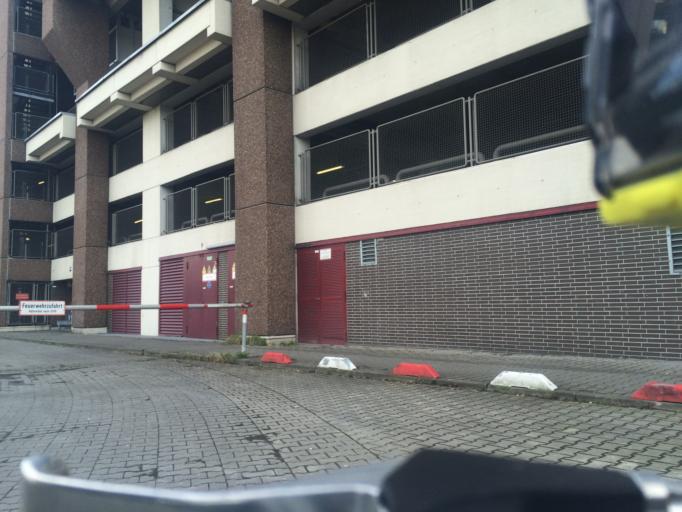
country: DE
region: Hesse
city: Kelsterbach
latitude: 50.0512
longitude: 8.5662
